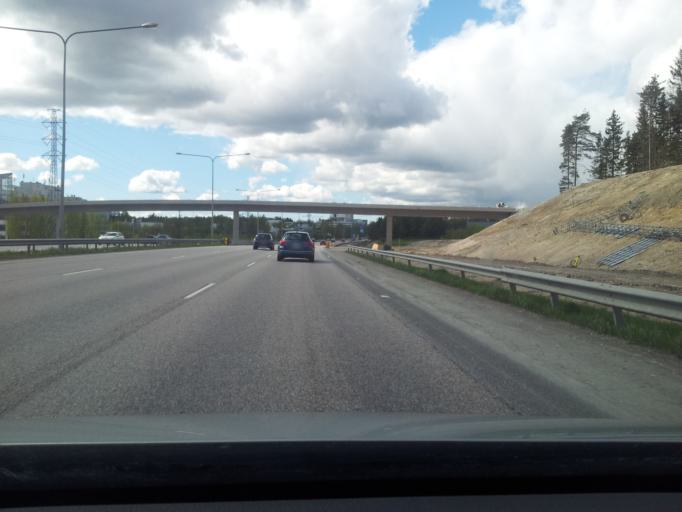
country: FI
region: Uusimaa
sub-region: Helsinki
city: Kilo
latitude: 60.2065
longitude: 24.7820
